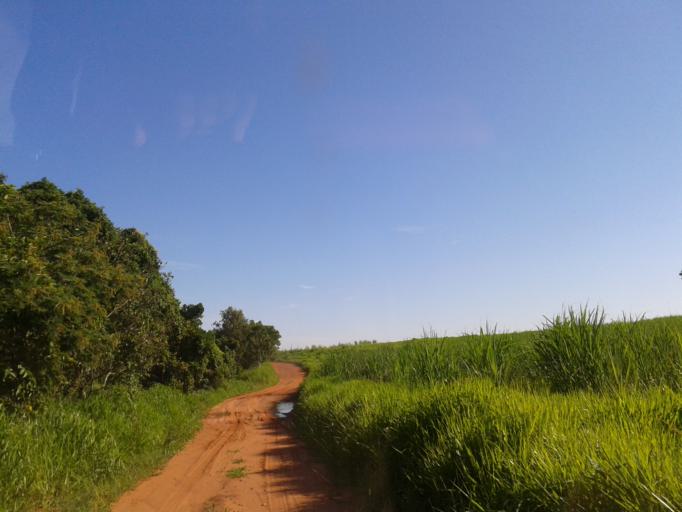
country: BR
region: Minas Gerais
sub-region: Santa Vitoria
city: Santa Vitoria
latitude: -19.1159
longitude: -49.9917
